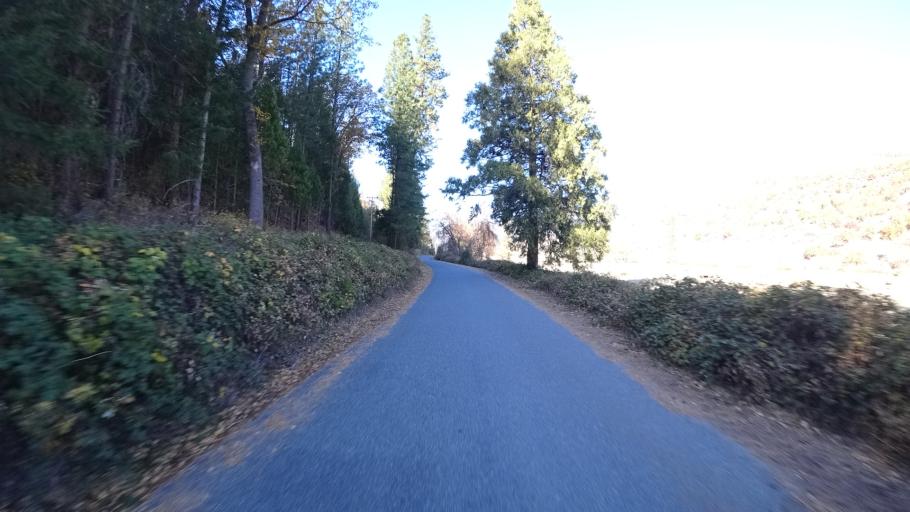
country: US
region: California
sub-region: Siskiyou County
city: Yreka
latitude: 41.8339
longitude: -122.8538
